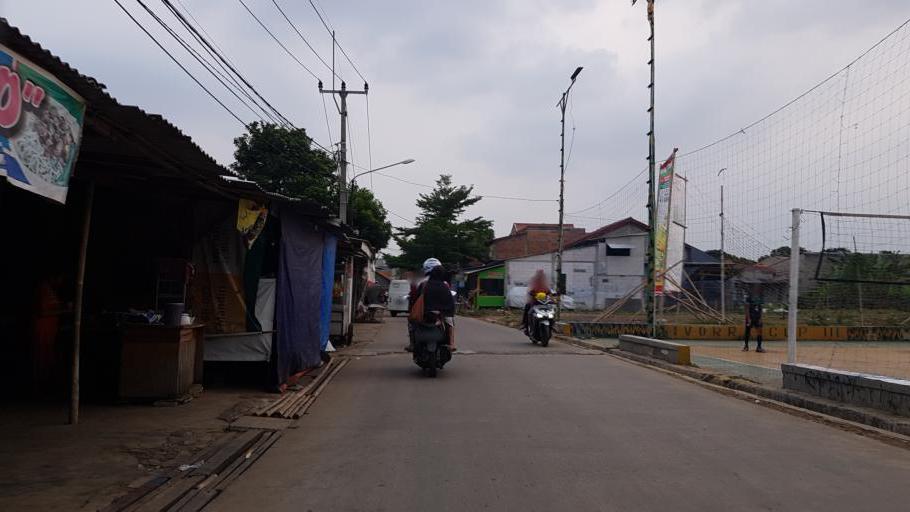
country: ID
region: West Java
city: Sawangan
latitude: -6.3768
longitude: 106.7947
